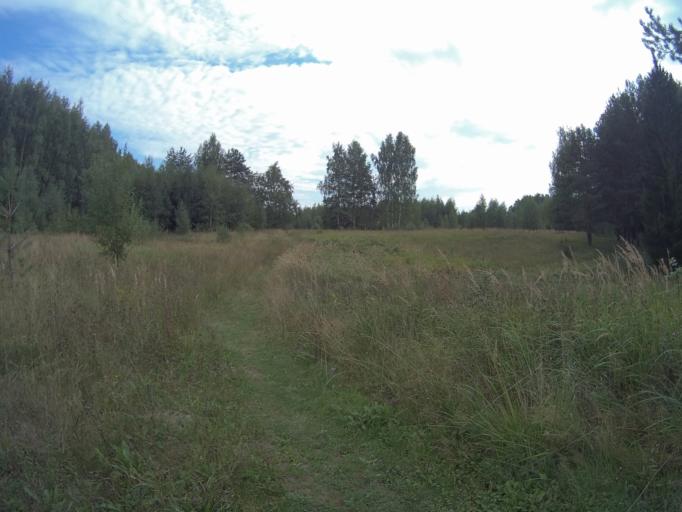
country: RU
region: Vladimir
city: Raduzhnyy
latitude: 56.0071
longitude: 40.3213
